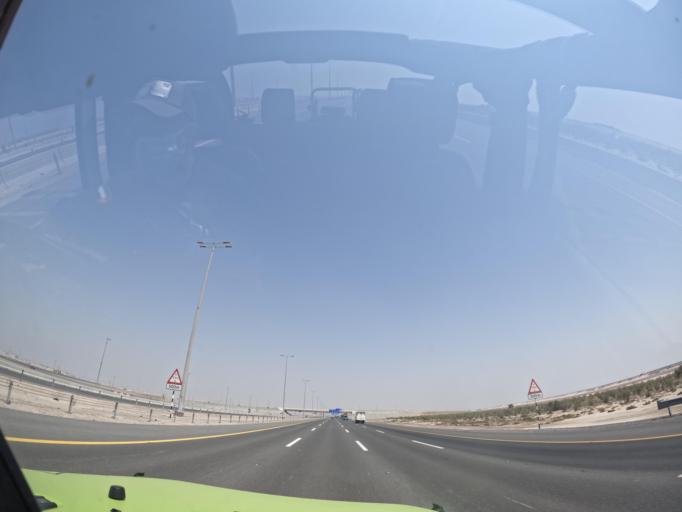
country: AE
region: Abu Dhabi
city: Abu Dhabi
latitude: 24.2762
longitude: 54.5191
